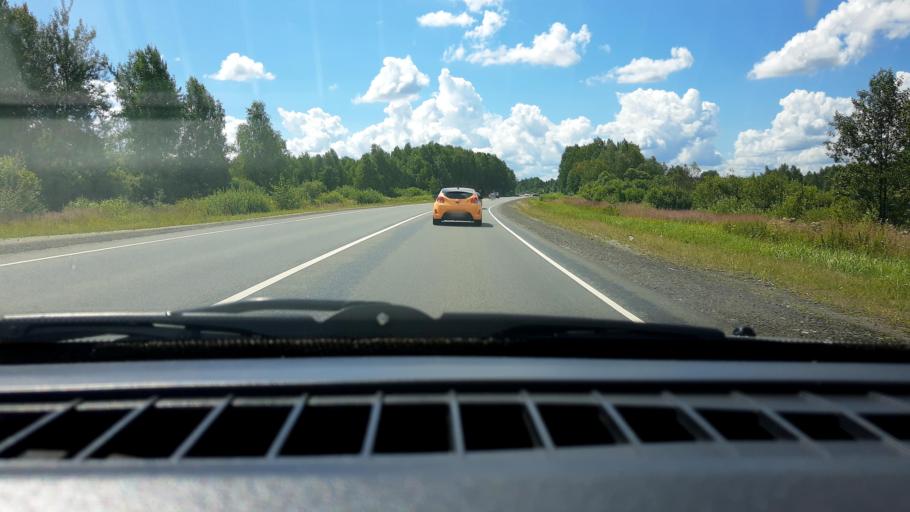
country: RU
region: Nizjnij Novgorod
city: Linda
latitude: 56.5875
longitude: 44.0331
